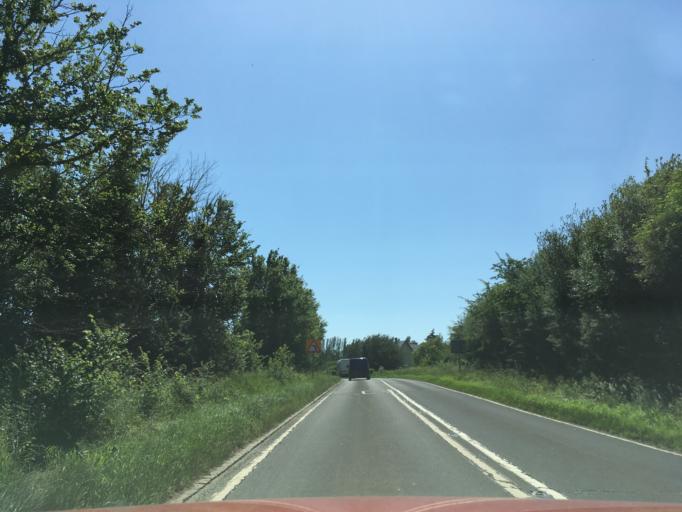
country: GB
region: England
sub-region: Northamptonshire
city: Brackley
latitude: 51.9971
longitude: -1.1799
